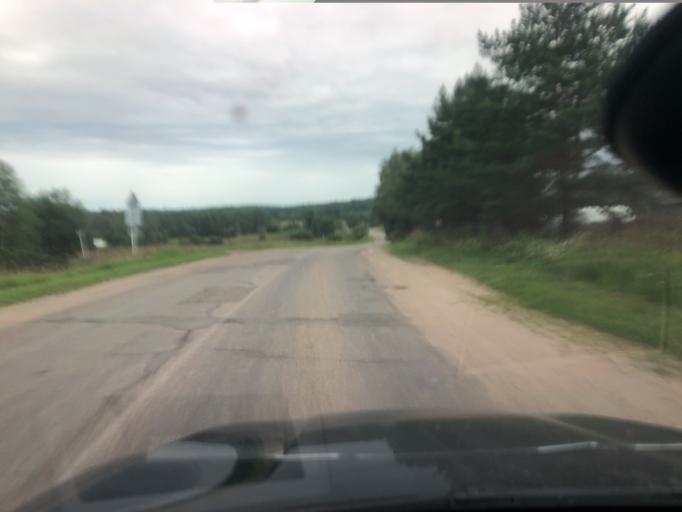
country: RU
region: Jaroslavl
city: Petrovsk
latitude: 56.9873
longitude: 39.1765
